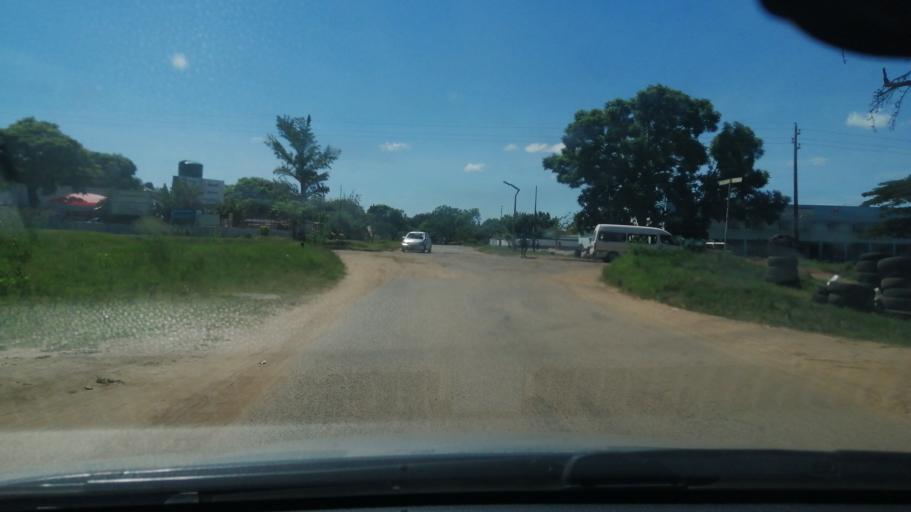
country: ZW
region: Harare
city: Epworth
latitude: -17.8192
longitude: 31.1303
